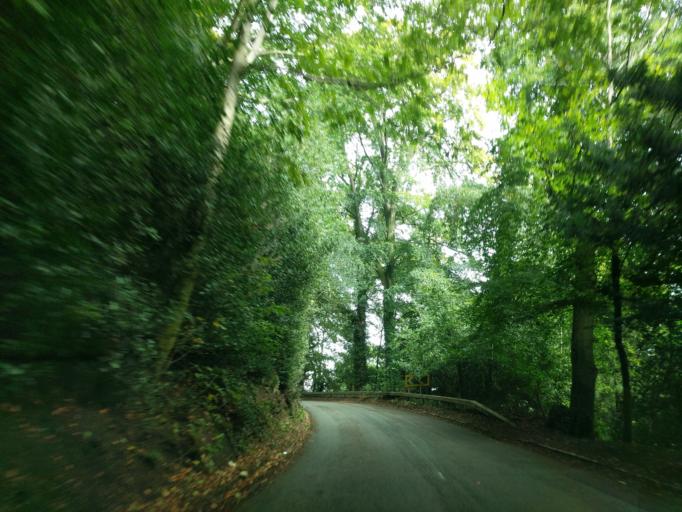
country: GB
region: England
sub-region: Staffordshire
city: Standon
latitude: 52.9694
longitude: -2.2835
